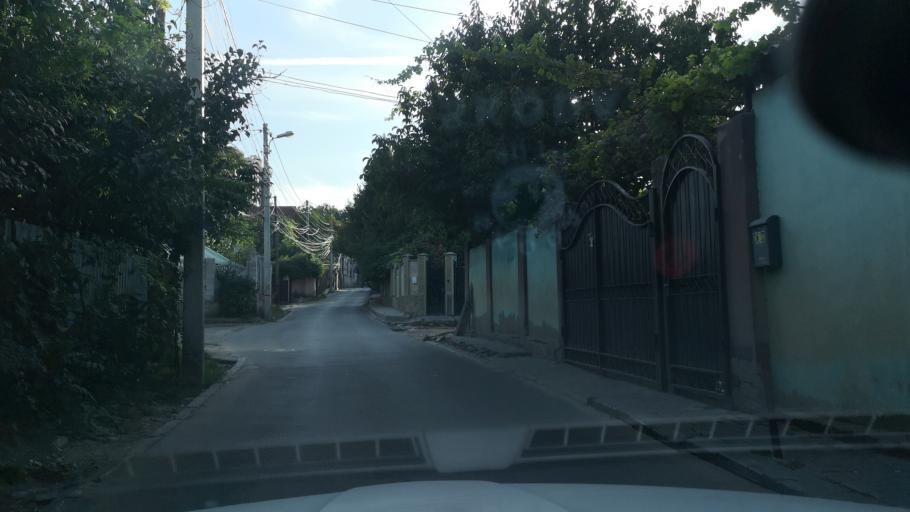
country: MD
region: Chisinau
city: Chisinau
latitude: 47.0081
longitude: 28.8562
